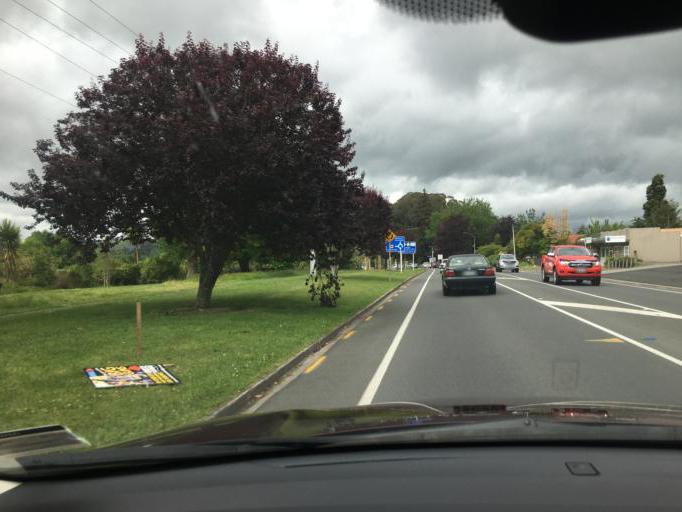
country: NZ
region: Waikato
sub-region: Waipa District
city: Cambridge
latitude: -37.9004
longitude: 175.4725
